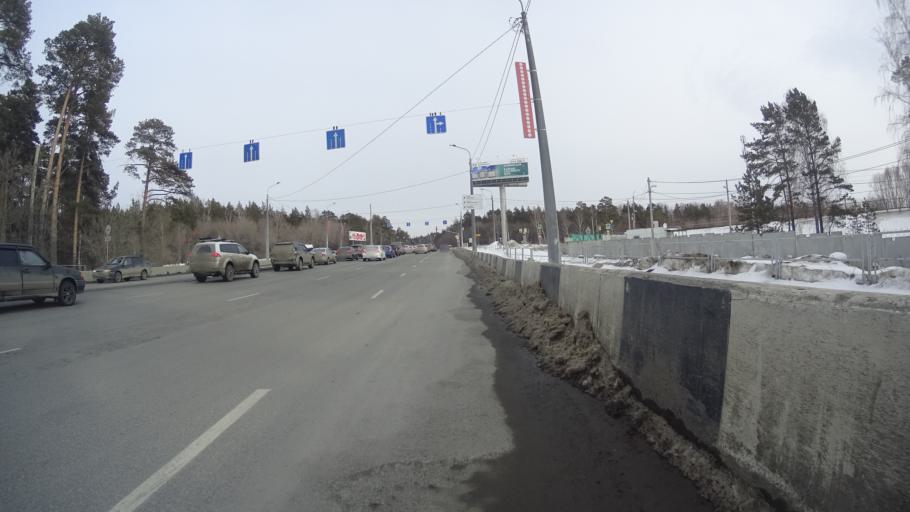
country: RU
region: Chelyabinsk
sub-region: Gorod Chelyabinsk
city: Chelyabinsk
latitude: 55.1475
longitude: 61.3278
